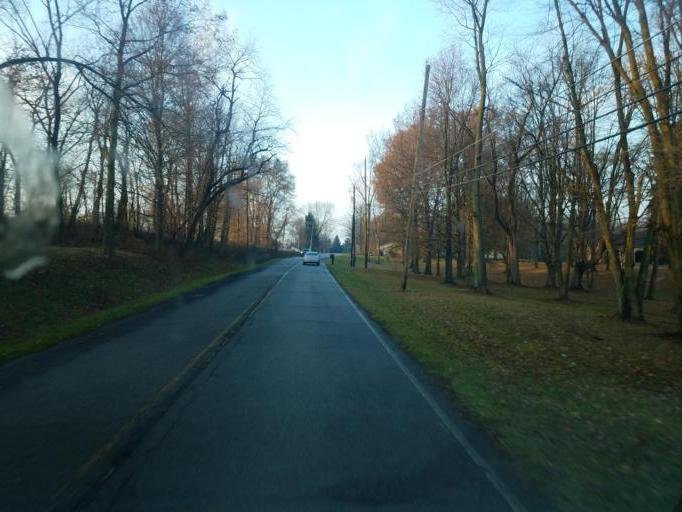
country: US
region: Ohio
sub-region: Knox County
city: Centerburg
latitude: 40.2431
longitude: -82.6892
